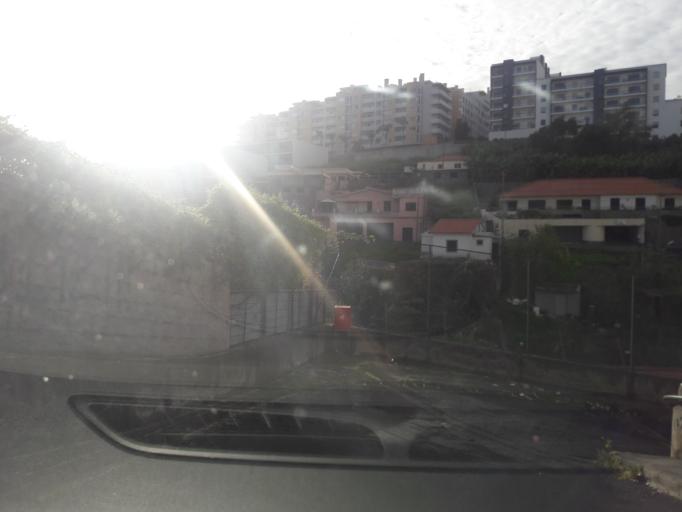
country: PT
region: Madeira
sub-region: Funchal
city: Nossa Senhora do Monte
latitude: 32.6558
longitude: -16.9287
